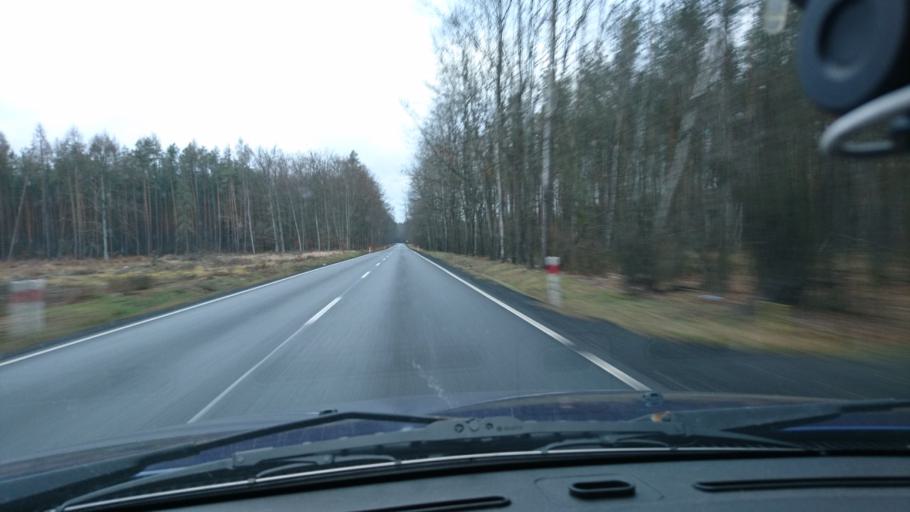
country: PL
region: Opole Voivodeship
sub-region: Powiat oleski
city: Olesno
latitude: 50.9311
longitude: 18.3335
